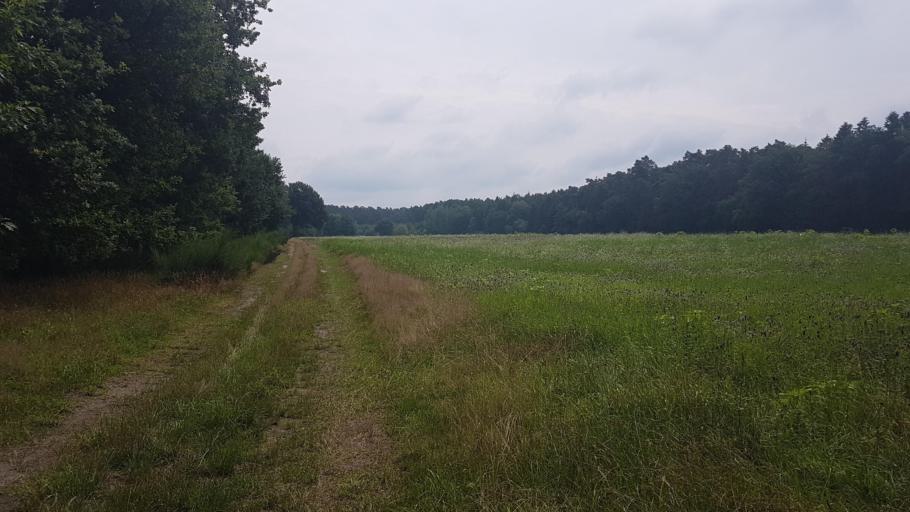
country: DE
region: Lower Saxony
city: Ludersburg
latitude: 53.2969
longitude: 10.5803
